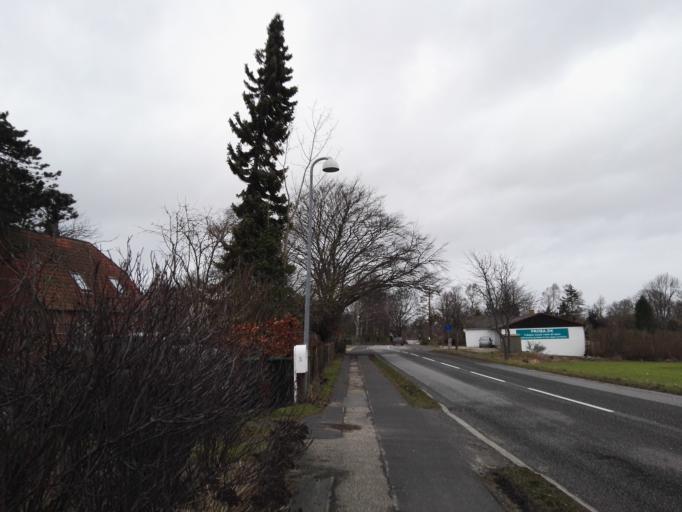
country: DK
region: Zealand
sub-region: Lejre Kommune
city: Ejby
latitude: 55.6905
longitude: 11.9115
